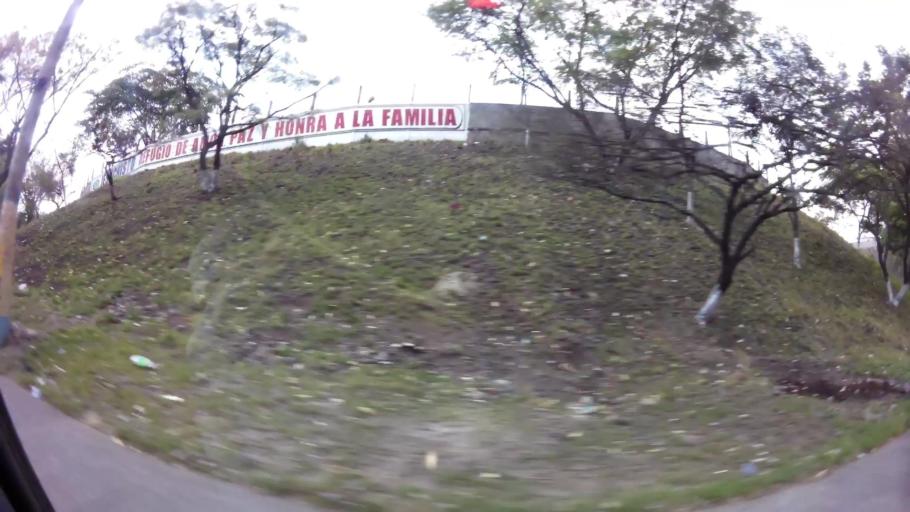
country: HN
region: Francisco Morazan
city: El Lolo
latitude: 14.1036
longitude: -87.2416
